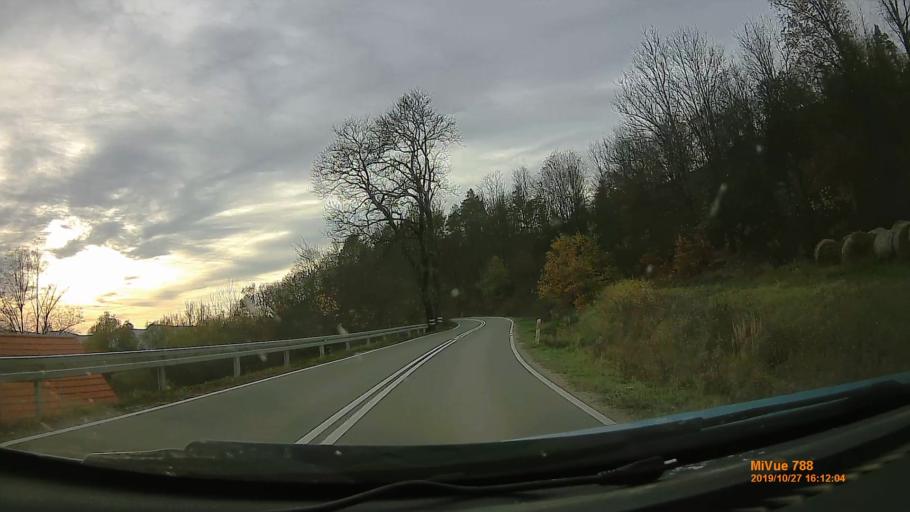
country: PL
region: Lower Silesian Voivodeship
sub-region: Powiat klodzki
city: Radkow
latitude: 50.5535
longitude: 16.4209
